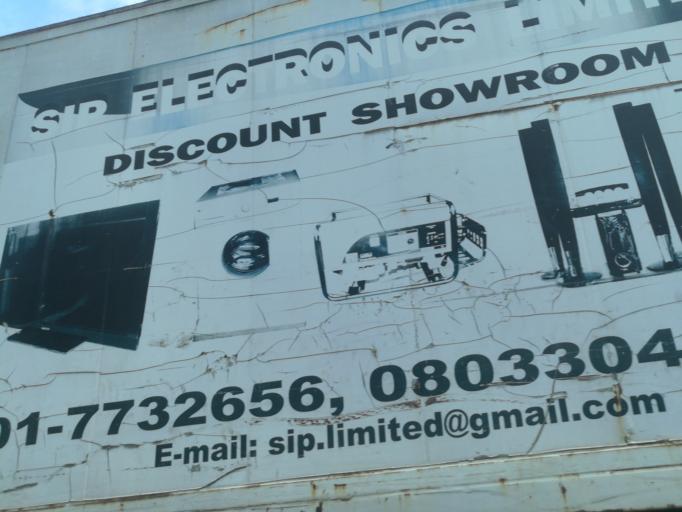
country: NG
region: Lagos
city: Ikeja
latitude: 6.6098
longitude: 3.3662
